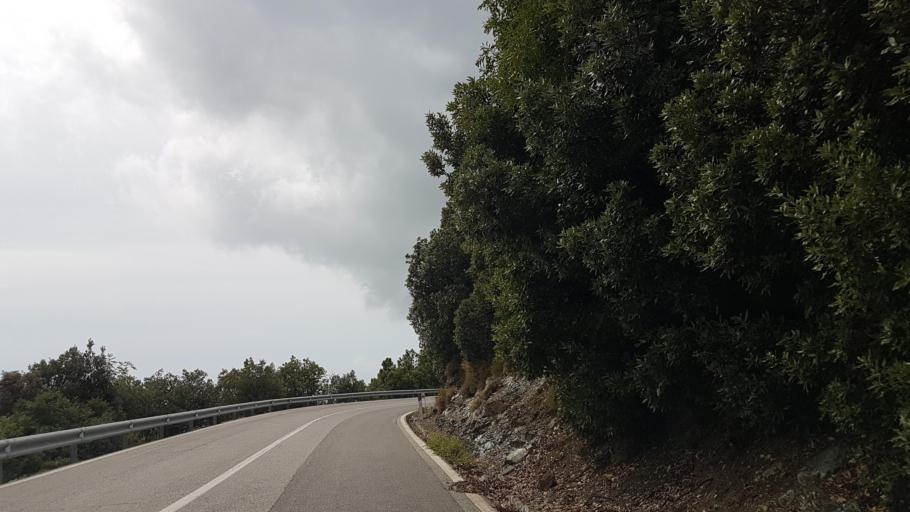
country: IT
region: Liguria
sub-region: Provincia di Genova
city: Castiglione
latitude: 44.2542
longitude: 9.5488
